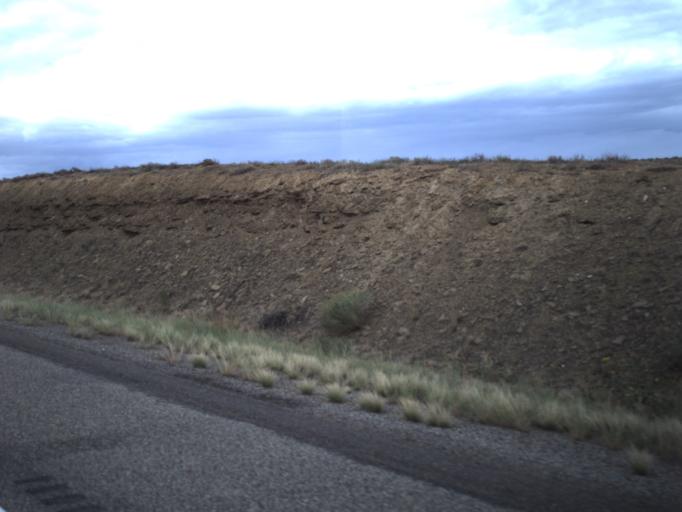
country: US
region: Colorado
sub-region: Mesa County
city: Loma
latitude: 39.1415
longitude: -109.1540
